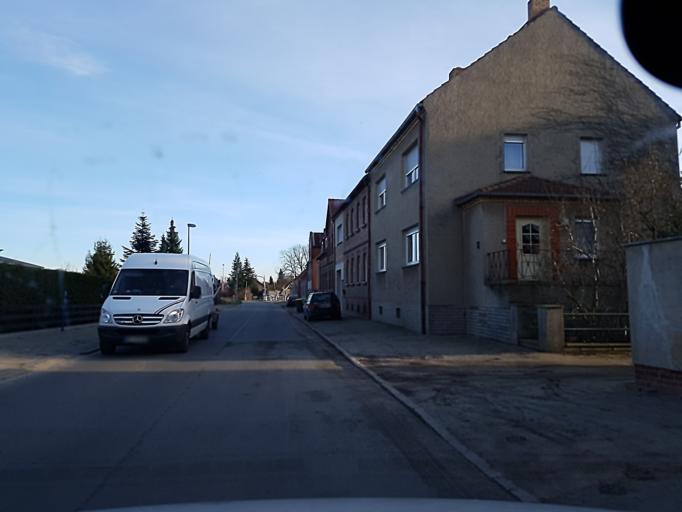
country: DE
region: Brandenburg
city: Finsterwalde
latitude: 51.6448
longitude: 13.7258
